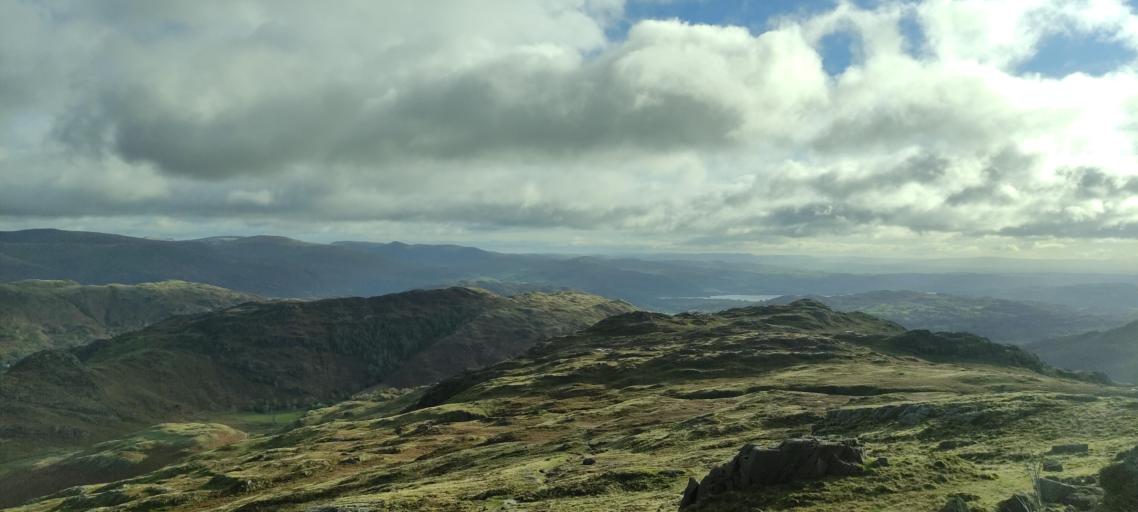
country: GB
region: England
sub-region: Cumbria
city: Ambleside
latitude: 54.4281
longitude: -3.1198
